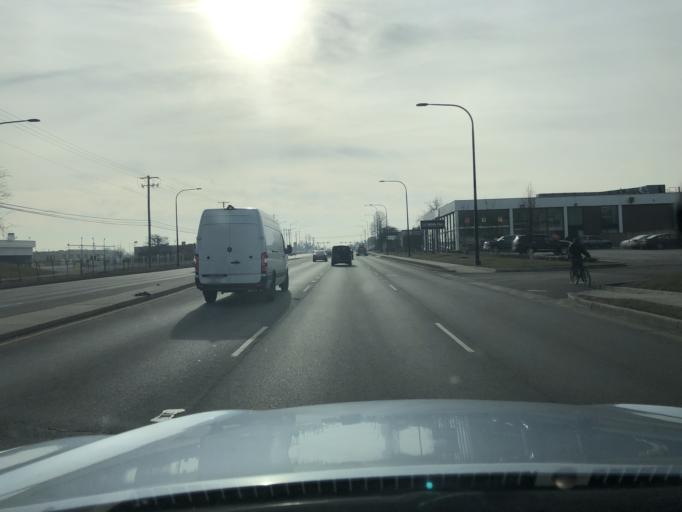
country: US
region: Illinois
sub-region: Cook County
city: Elk Grove Village
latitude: 42.0118
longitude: -87.9404
